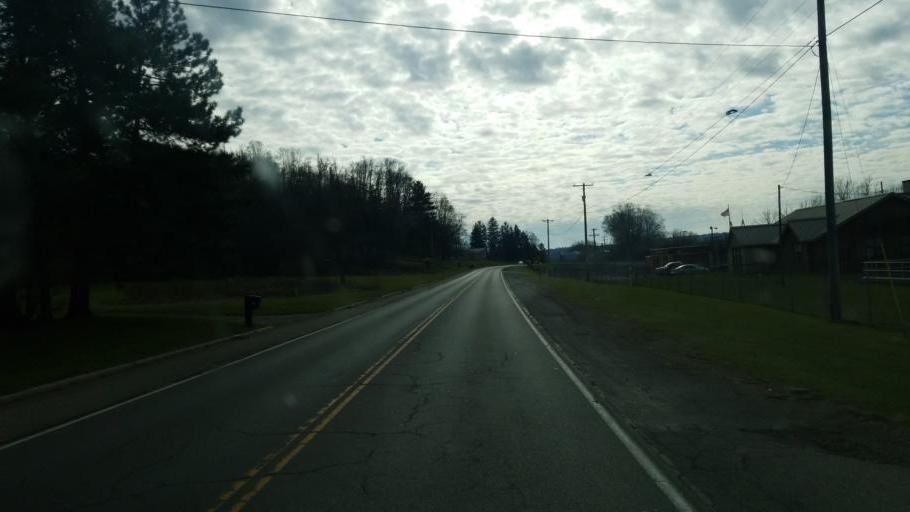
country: US
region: Ohio
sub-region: Richland County
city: Lexington
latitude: 40.7041
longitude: -82.5822
